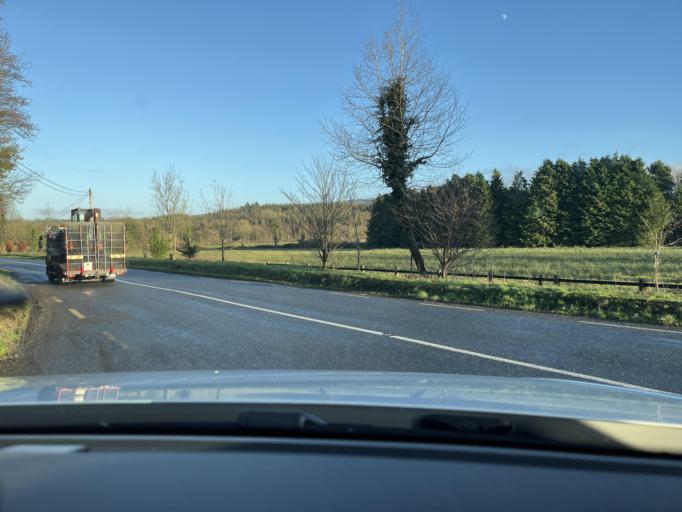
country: IE
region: Ulster
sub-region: An Cabhan
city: Ballyconnell
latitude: 54.1524
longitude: -7.7199
